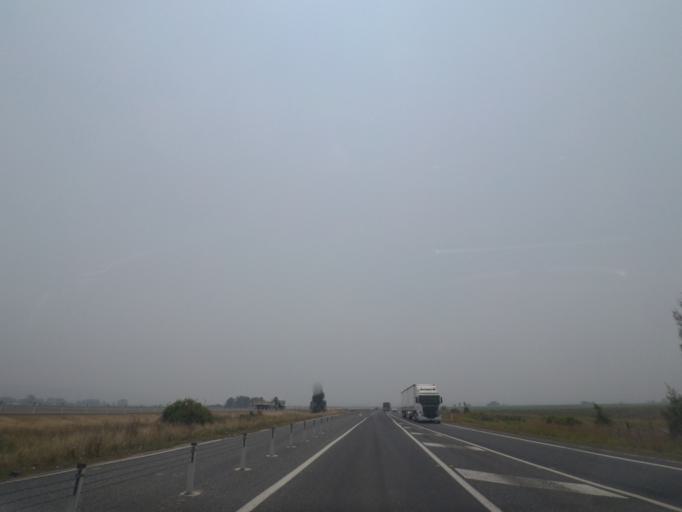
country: AU
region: New South Wales
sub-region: Clarence Valley
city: Maclean
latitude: -29.3902
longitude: 153.2402
